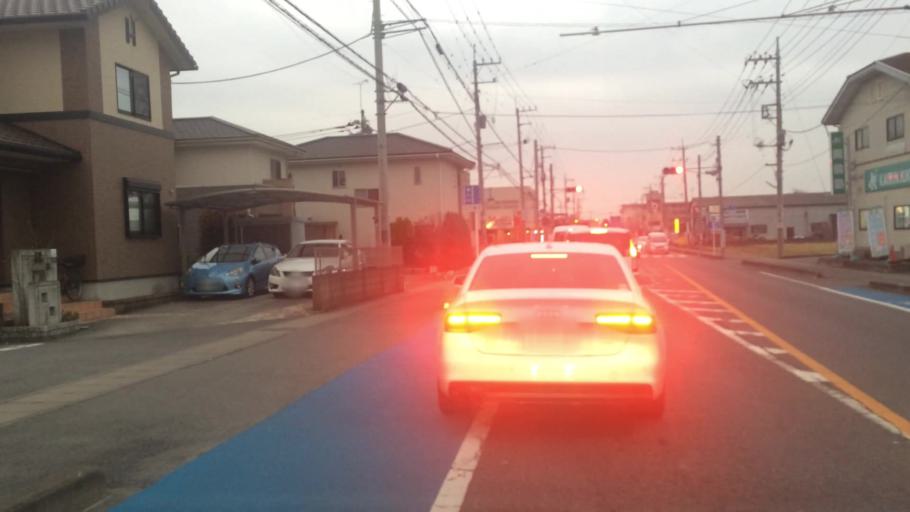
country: JP
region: Tochigi
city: Utsunomiya-shi
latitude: 36.5932
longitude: 139.8537
